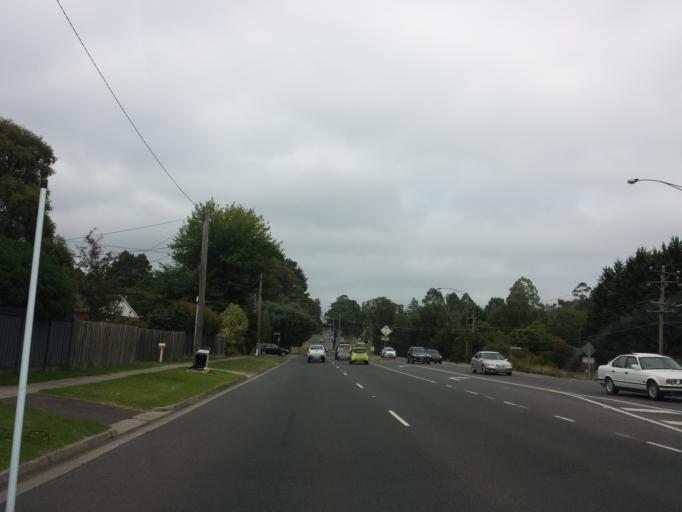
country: AU
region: Victoria
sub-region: Yarra Ranges
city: Montrose
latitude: -37.8067
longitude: 145.3510
